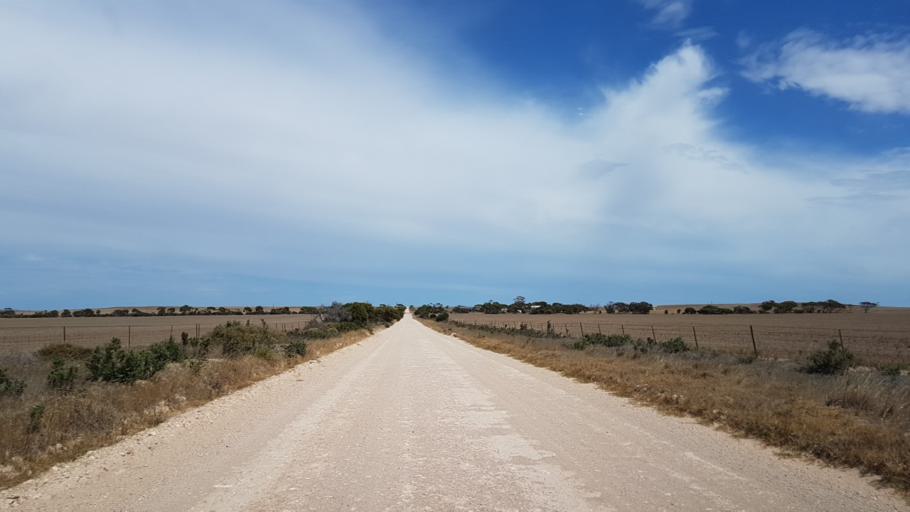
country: AU
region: South Australia
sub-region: Yorke Peninsula
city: Ardrossan
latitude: -34.3984
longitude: 137.9243
